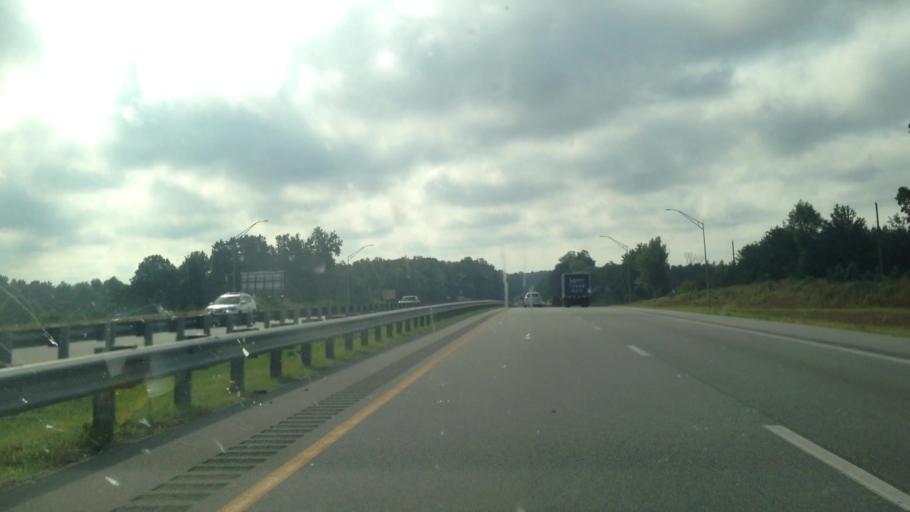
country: US
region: North Carolina
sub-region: Forsyth County
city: Kernersville
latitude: 36.1062
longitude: -80.0443
